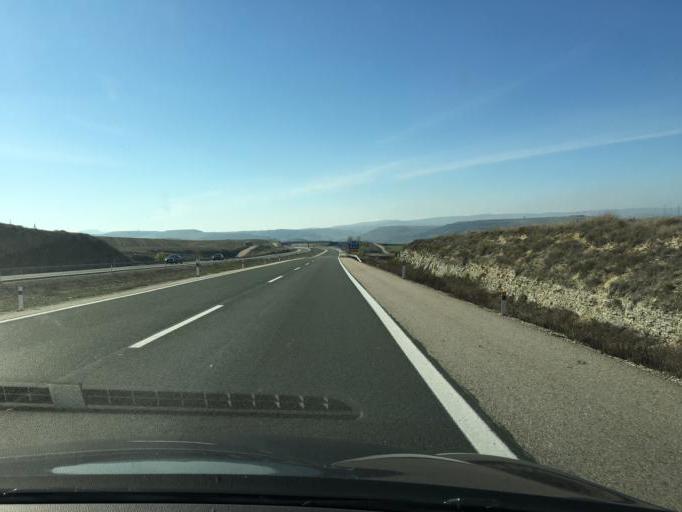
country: ES
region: Castille and Leon
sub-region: Provincia de Burgos
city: Briviesca
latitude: 42.5411
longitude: -3.2995
